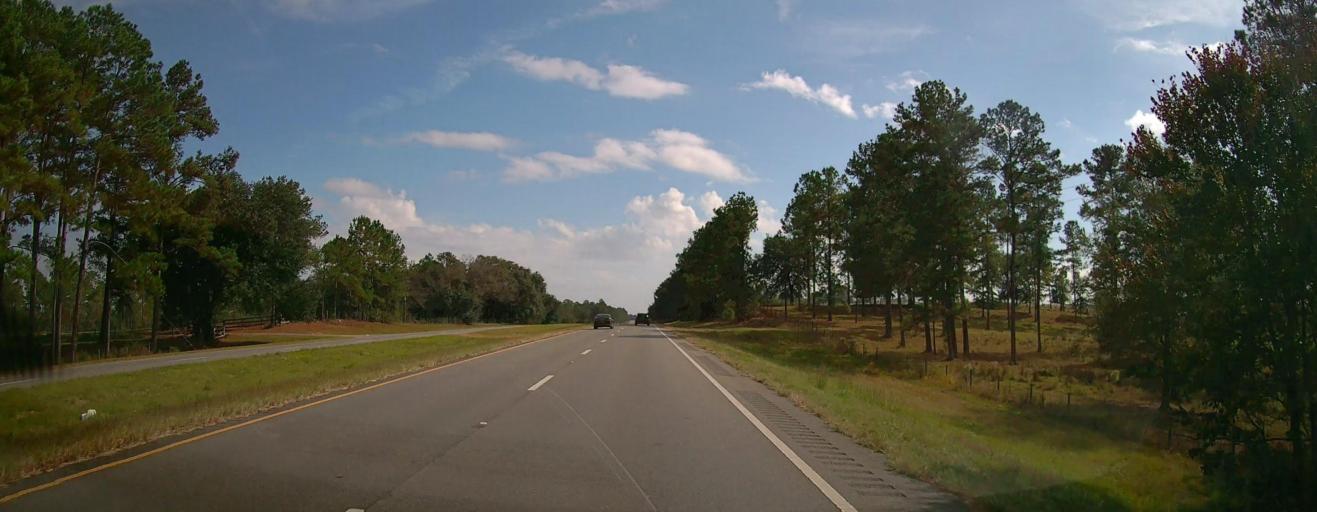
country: US
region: Georgia
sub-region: Thomas County
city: Meigs
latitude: 30.9652
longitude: -84.0316
